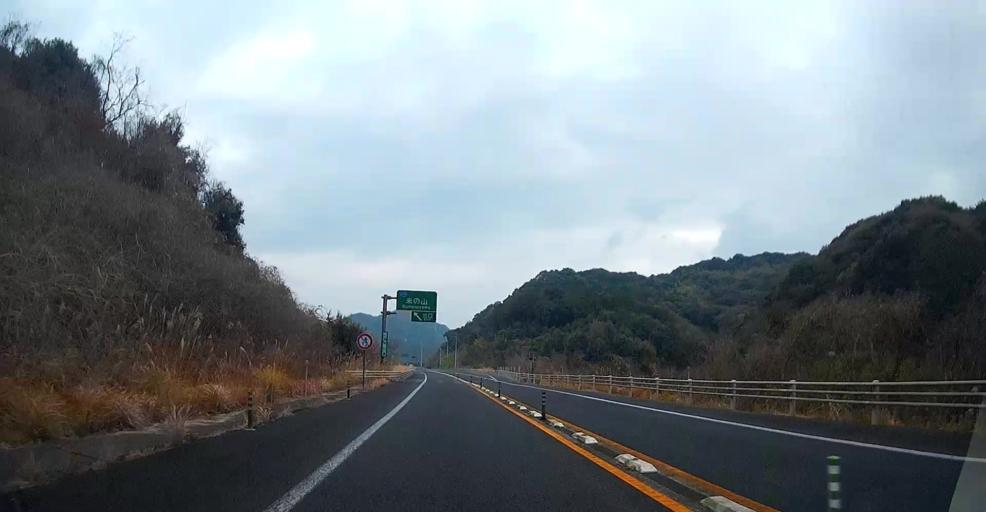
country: JP
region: Kumamoto
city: Hondo
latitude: 32.4974
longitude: 130.3864
